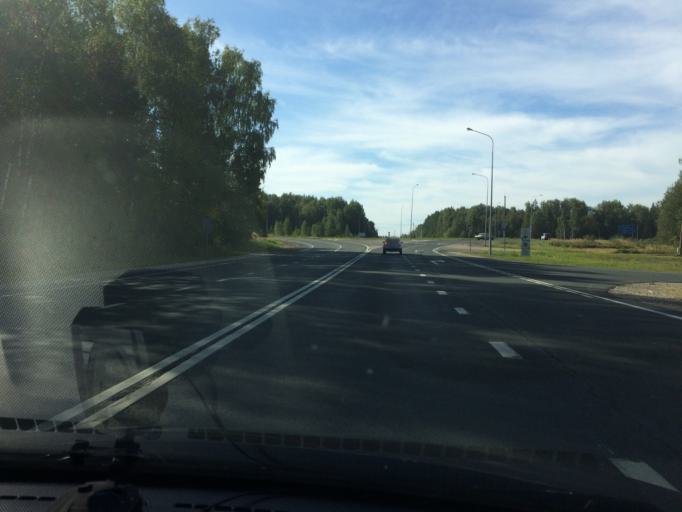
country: RU
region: Mariy-El
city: Yoshkar-Ola
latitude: 56.5849
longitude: 47.9730
